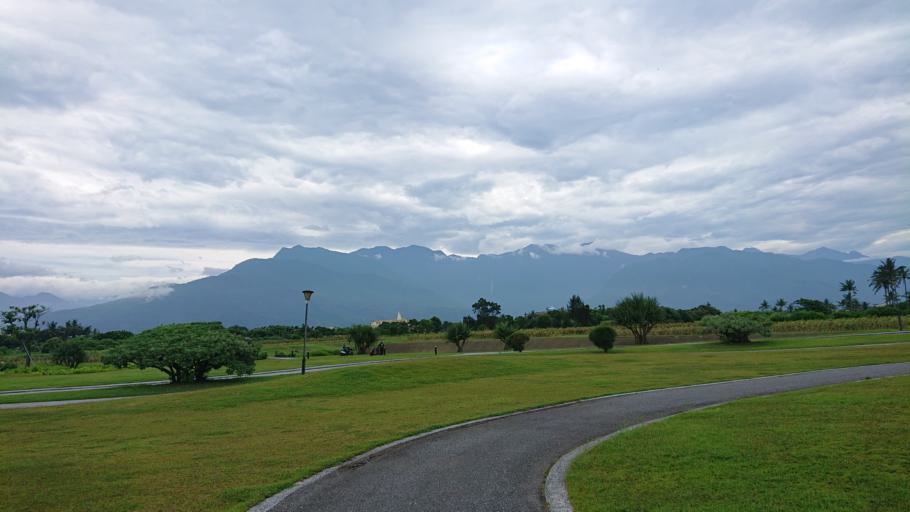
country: TW
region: Taiwan
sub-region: Hualien
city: Hualian
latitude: 23.9383
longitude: 121.6027
